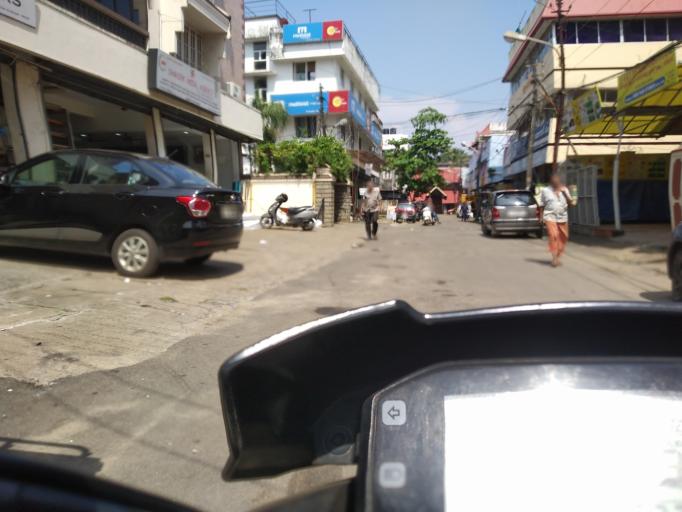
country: IN
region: Kerala
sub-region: Ernakulam
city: Cochin
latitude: 9.9794
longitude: 76.2792
